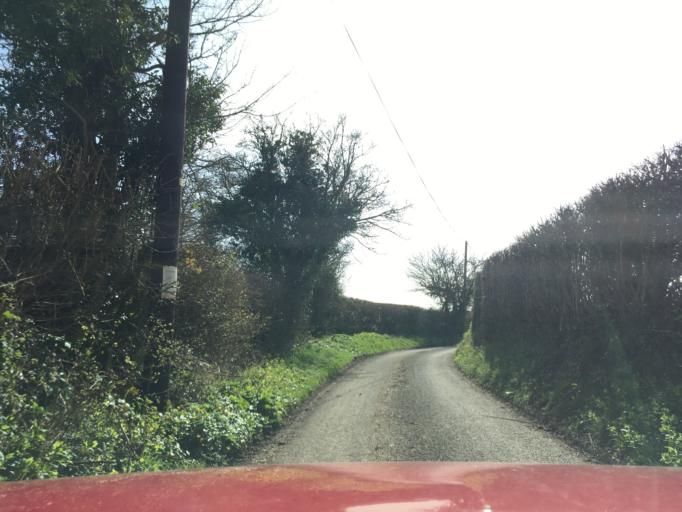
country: GB
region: England
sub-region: Wiltshire
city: Chippenham
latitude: 51.4983
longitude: -2.1500
